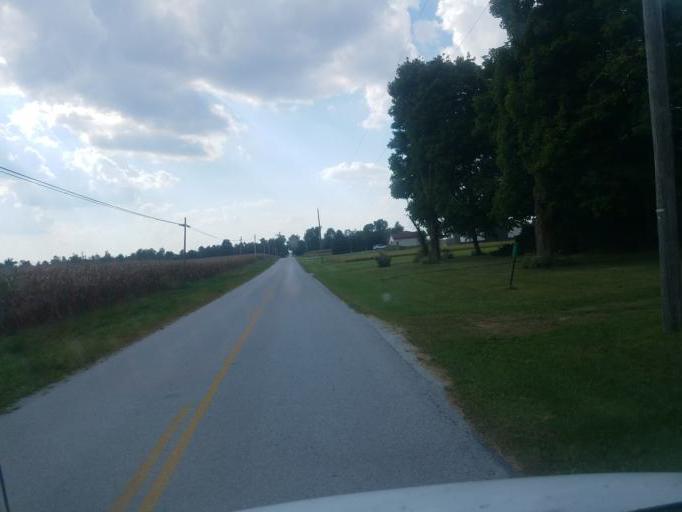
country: US
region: Ohio
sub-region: Hancock County
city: Arlington
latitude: 40.7906
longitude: -83.6727
